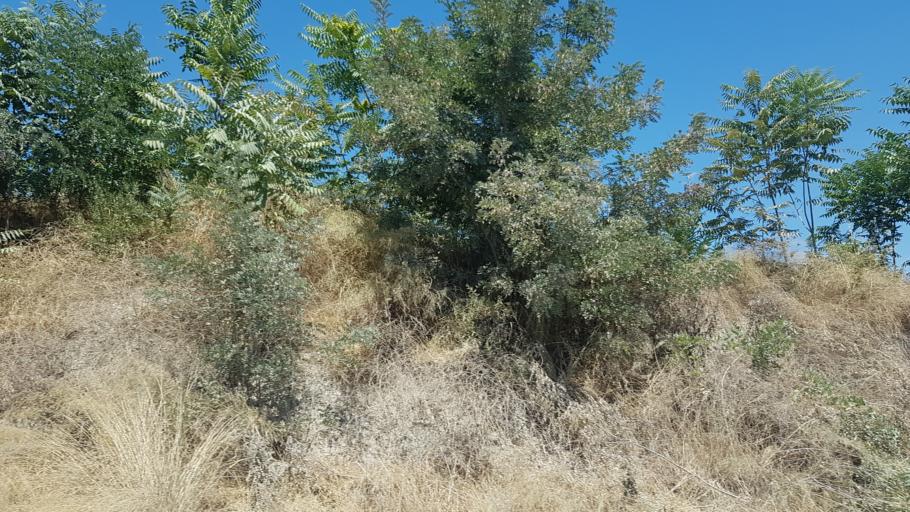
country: TR
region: Mugla
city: Turgut
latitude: 37.3190
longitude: 28.0734
